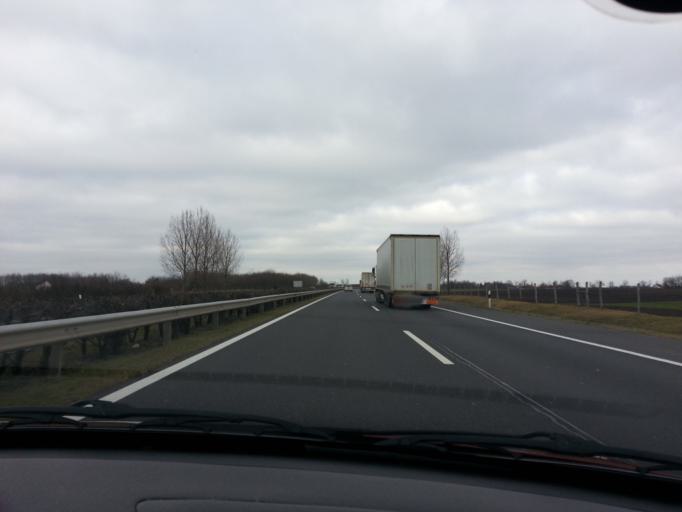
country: HU
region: Bacs-Kiskun
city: Kiskunfelegyhaza
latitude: 46.6957
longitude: 19.8072
